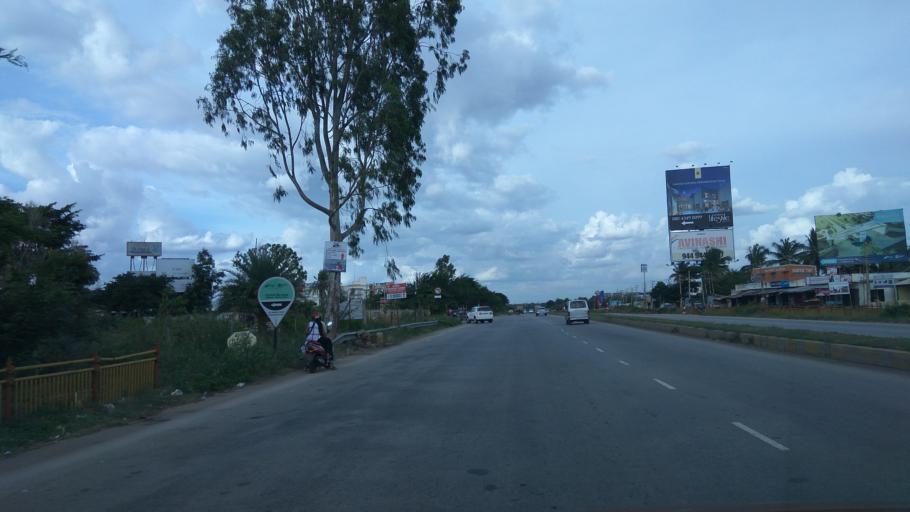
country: IN
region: Karnataka
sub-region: Bangalore Rural
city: Devanhalli
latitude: 13.2257
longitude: 77.6864
